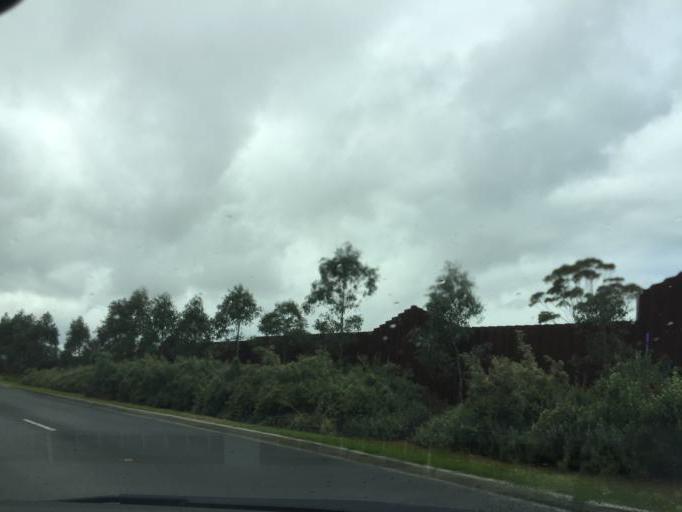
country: AU
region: Victoria
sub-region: Brimbank
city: Sunshine West
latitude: -37.7848
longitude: 144.8220
